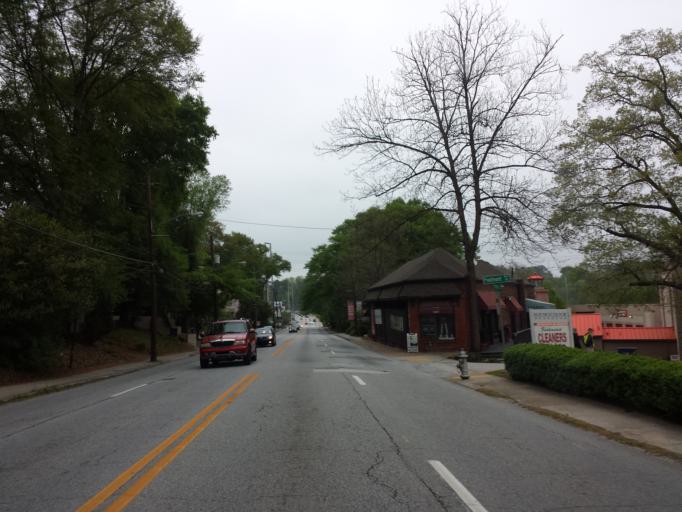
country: US
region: Georgia
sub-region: DeKalb County
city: Druid Hills
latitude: 33.7937
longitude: -84.3723
